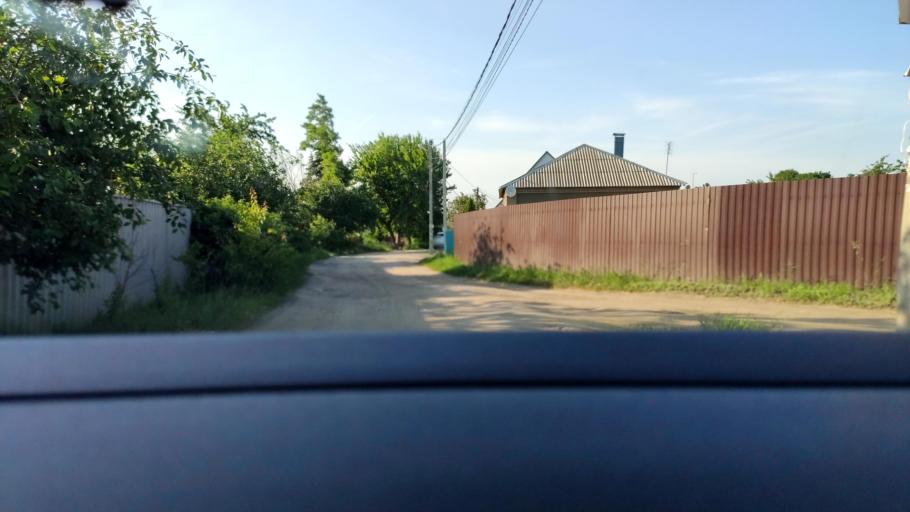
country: RU
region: Voronezj
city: Podgornoye
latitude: 51.7296
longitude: 39.1430
